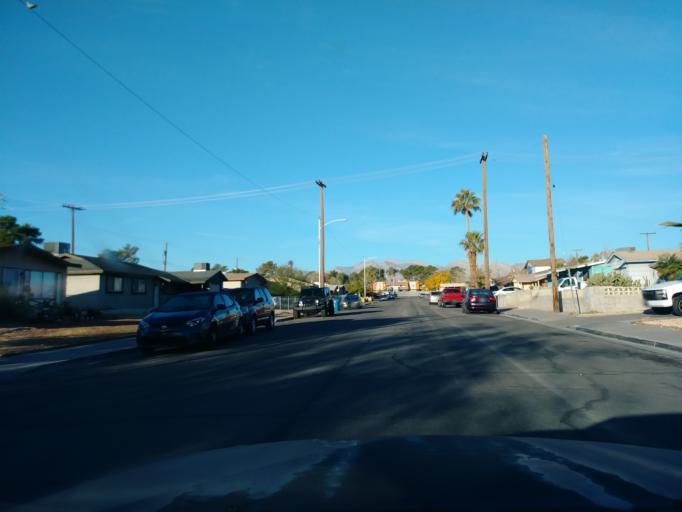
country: US
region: Nevada
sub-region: Clark County
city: Spring Valley
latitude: 36.1608
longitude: -115.2370
